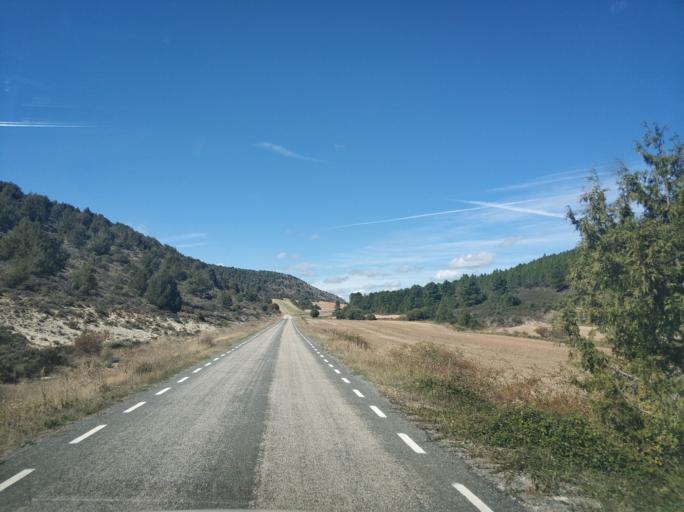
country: ES
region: Castille and Leon
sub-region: Provincia de Soria
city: Espeja de San Marcelino
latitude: 41.8151
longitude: -3.2315
